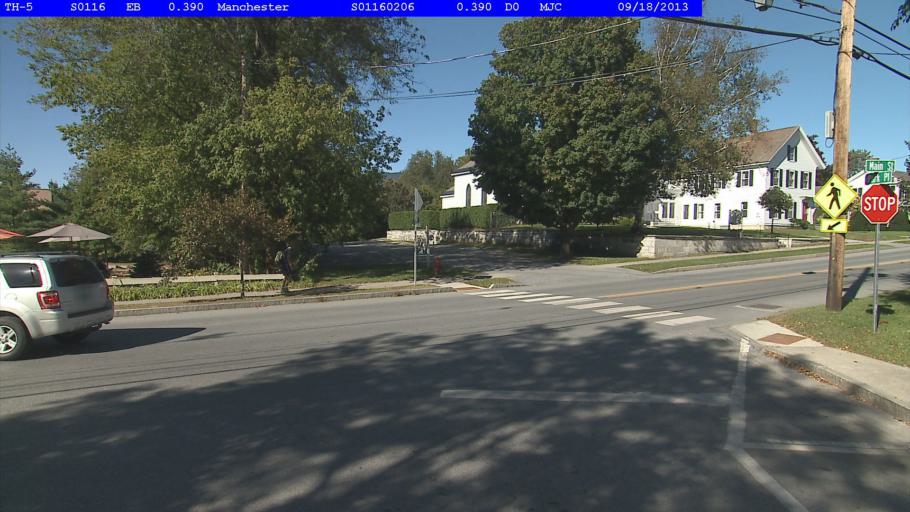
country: US
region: Vermont
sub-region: Bennington County
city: Manchester Center
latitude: 43.1777
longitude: -73.0525
